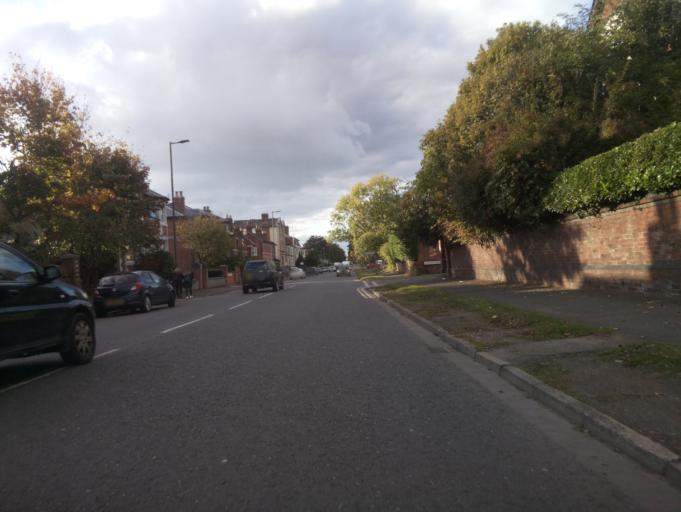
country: GB
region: England
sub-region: Herefordshire
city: Belmont
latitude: 52.0607
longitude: -2.7371
